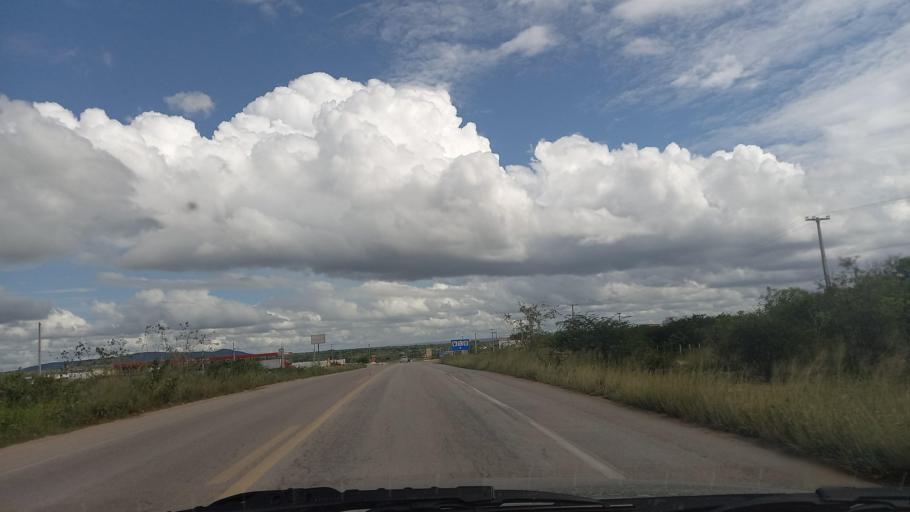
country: BR
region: Pernambuco
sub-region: Cachoeirinha
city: Cachoeirinha
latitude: -8.4787
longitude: -36.2234
